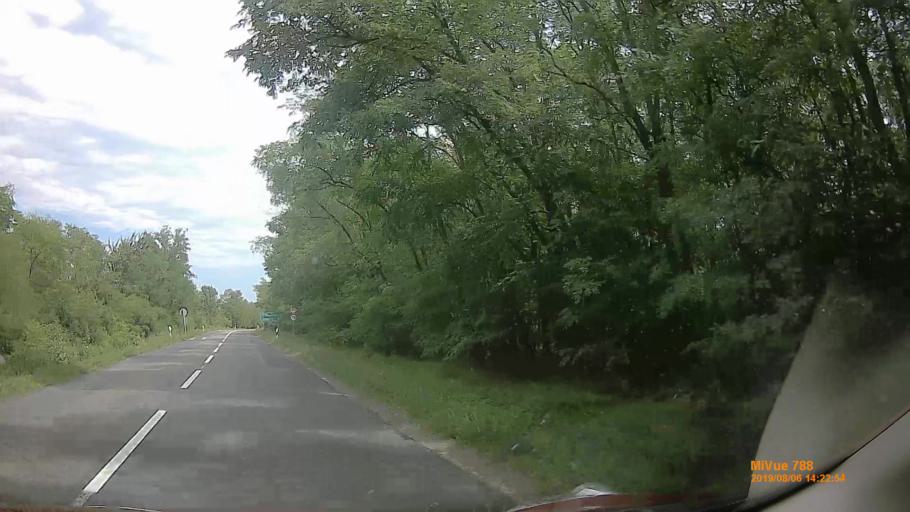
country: HU
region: Vas
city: Vep
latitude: 47.1583
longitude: 16.7995
